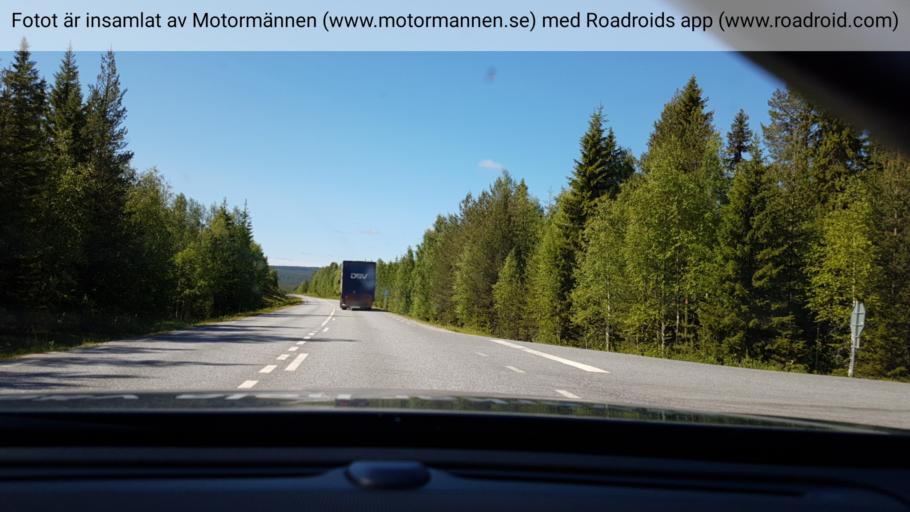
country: SE
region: Vaesterbotten
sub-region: Asele Kommun
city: Asele
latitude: 64.1978
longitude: 17.4967
